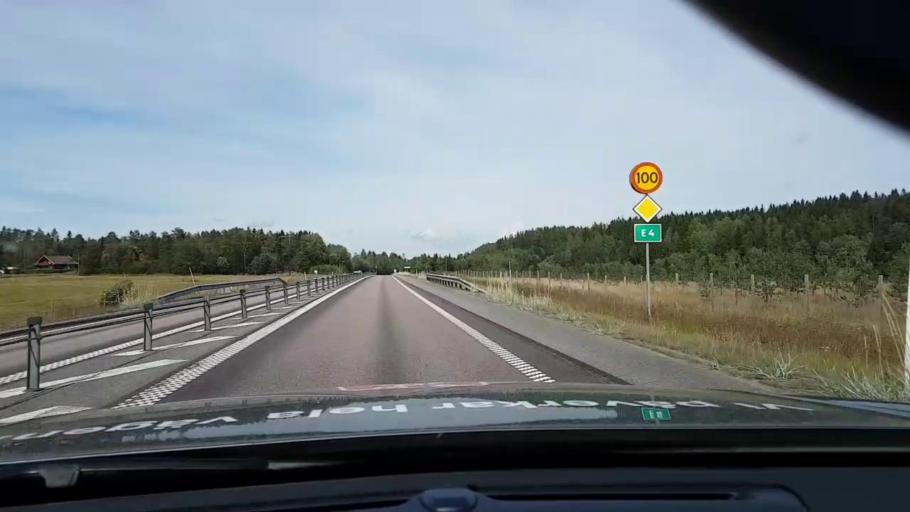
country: SE
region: Vaesternorrland
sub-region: OErnskoeldsviks Kommun
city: Husum
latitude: 63.4165
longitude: 19.2058
